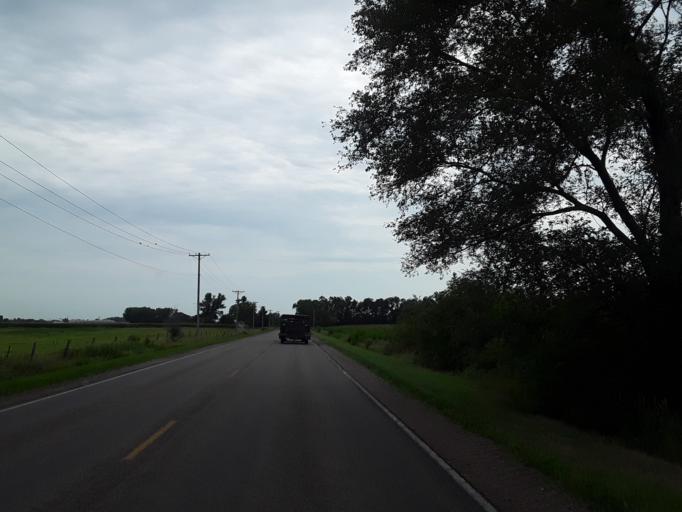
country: US
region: Nebraska
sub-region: Saunders County
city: Yutan
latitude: 41.2456
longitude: -96.3304
